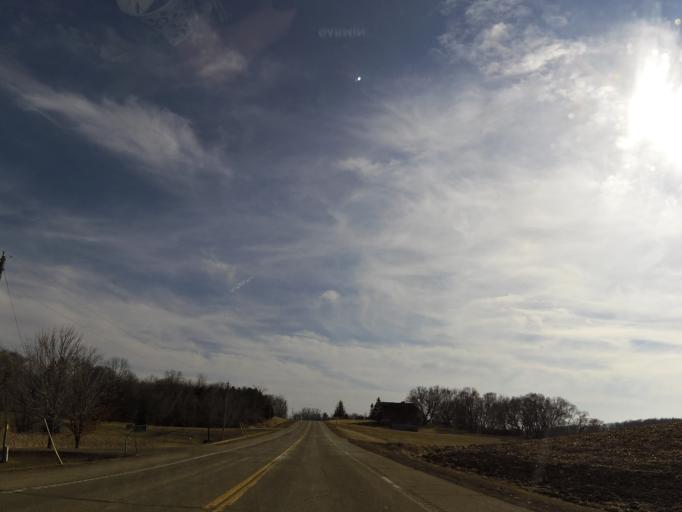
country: US
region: Minnesota
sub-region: Scott County
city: Prior Lake
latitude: 44.6411
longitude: -93.4705
